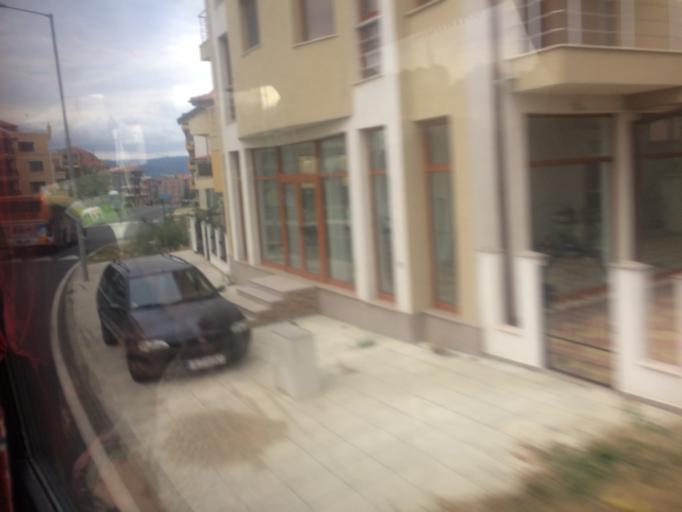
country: BG
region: Burgas
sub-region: Obshtina Nesebur
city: Ravda
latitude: 42.6613
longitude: 27.7021
